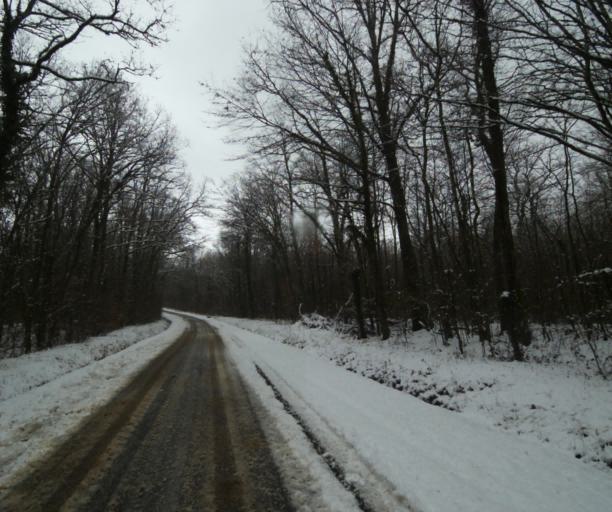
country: FR
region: Champagne-Ardenne
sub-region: Departement de la Haute-Marne
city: Wassy
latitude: 48.4551
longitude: 4.9412
